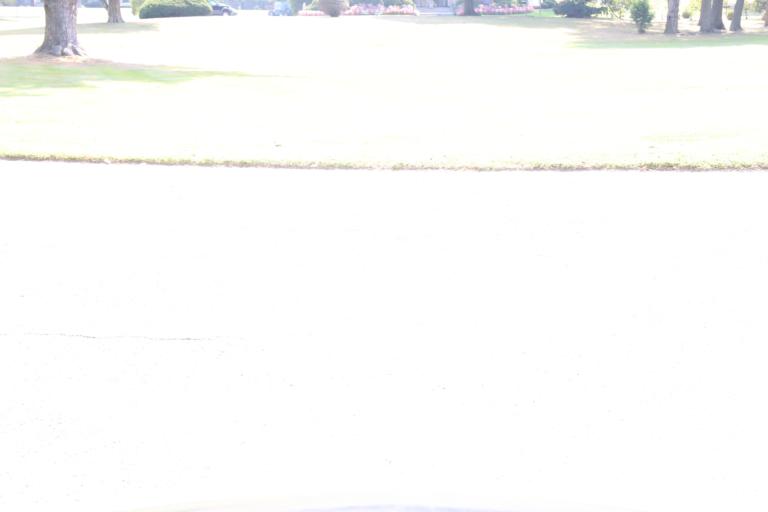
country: US
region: New York
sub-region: Bronx
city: The Bronx
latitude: 40.8888
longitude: -73.8773
